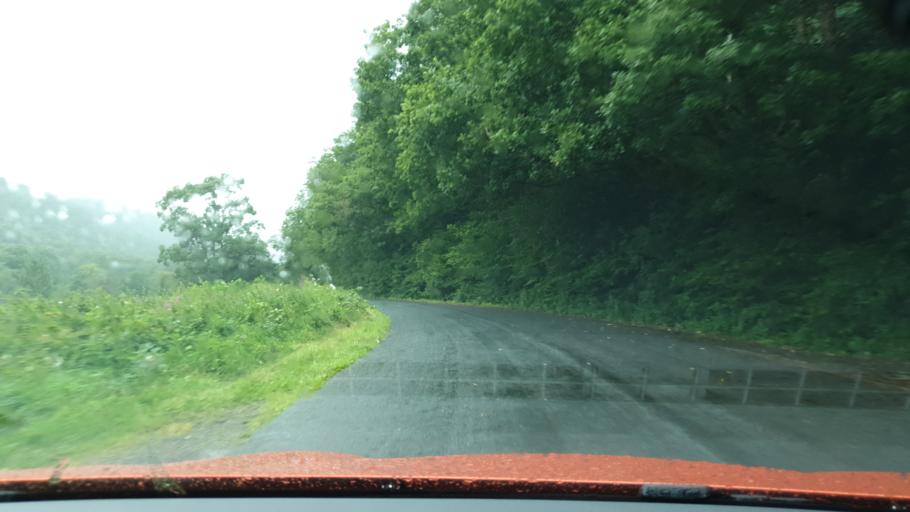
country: GB
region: England
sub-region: Cumbria
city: Millom
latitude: 54.2844
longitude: -3.2314
